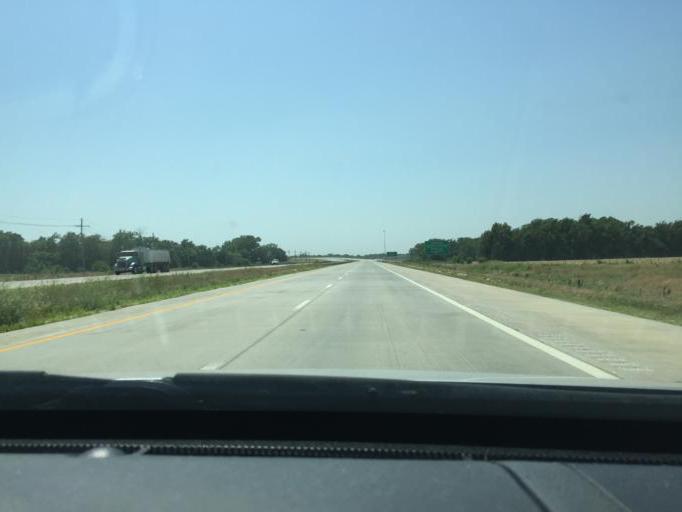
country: US
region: Kansas
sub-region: Reno County
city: South Hutchinson
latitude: 38.0290
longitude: -97.8910
